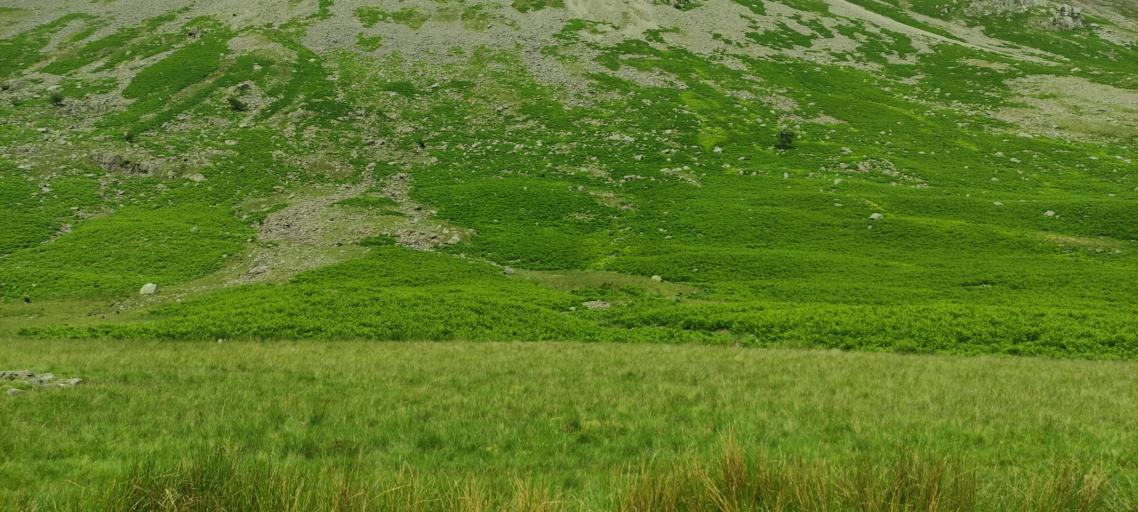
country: GB
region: England
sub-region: Cumbria
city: Keswick
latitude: 54.4503
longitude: -3.1298
